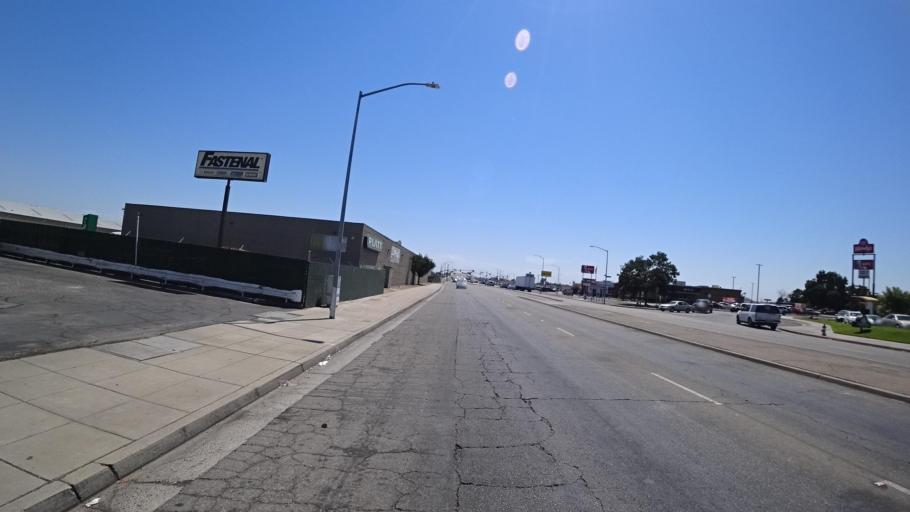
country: US
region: California
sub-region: Fresno County
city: Fresno
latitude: 36.7069
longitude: -119.7713
